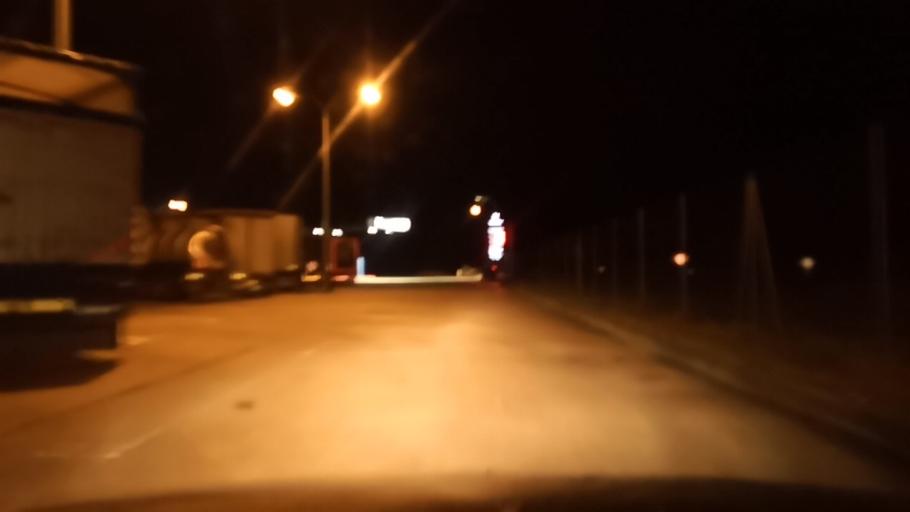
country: ES
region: Castille and Leon
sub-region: Provincia de Salamanca
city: Ciudad Rodrigo
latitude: 40.6161
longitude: -6.5148
